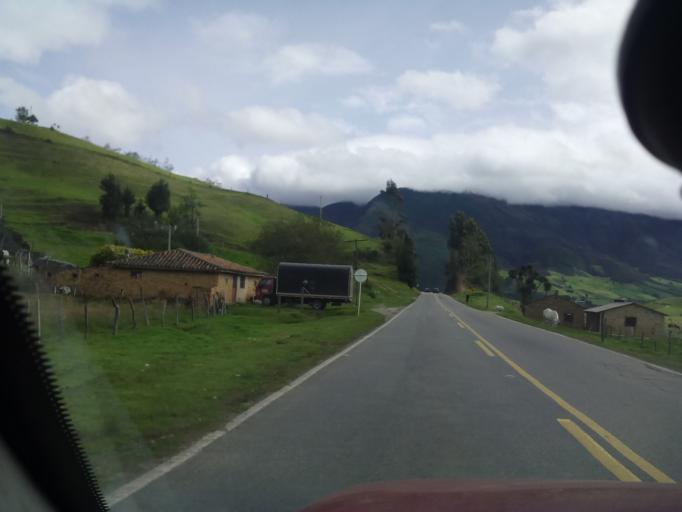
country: CO
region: Boyaca
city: Combita
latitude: 5.6984
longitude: -73.3687
